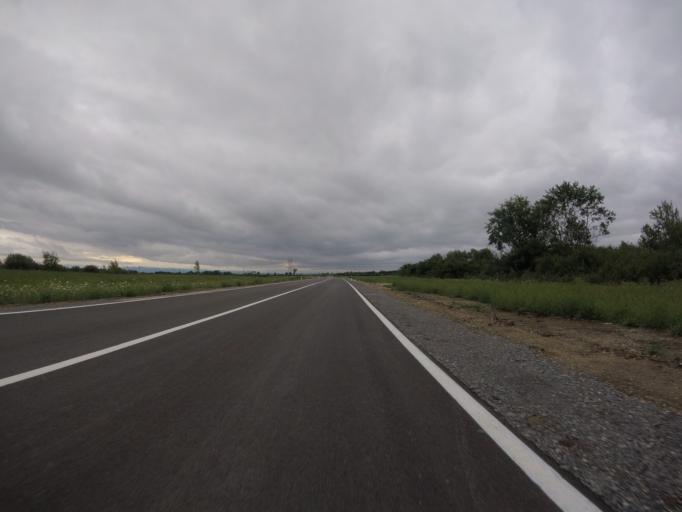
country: HR
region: Zagrebacka
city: Mraclin
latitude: 45.6541
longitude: 16.1164
